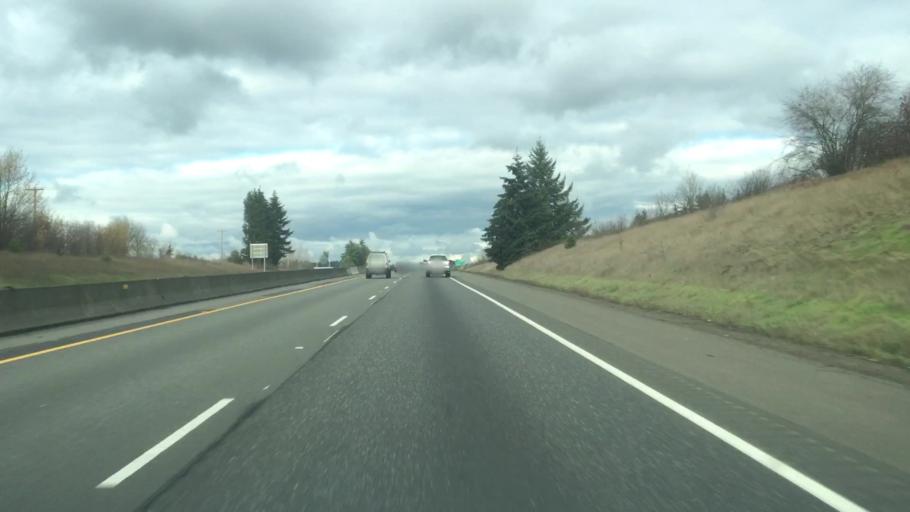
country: US
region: Washington
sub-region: Lewis County
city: Winlock
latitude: 46.4491
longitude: -122.8871
